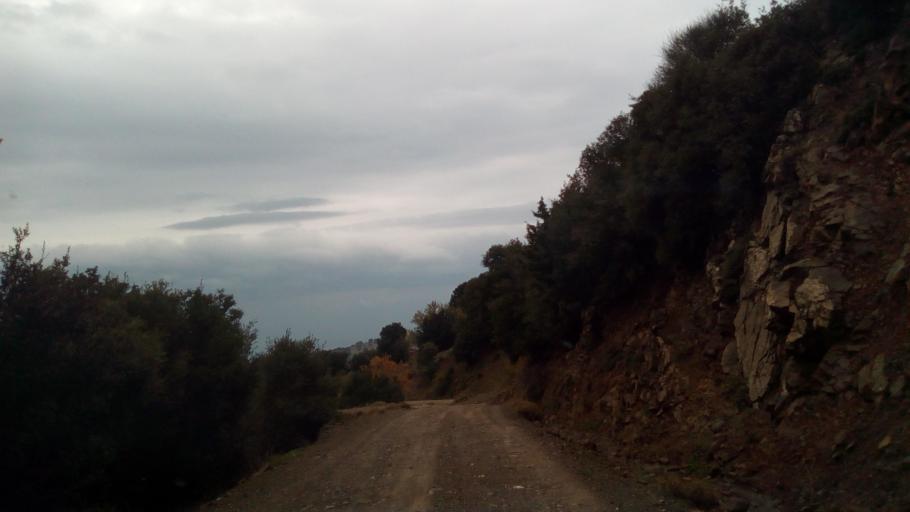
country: GR
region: West Greece
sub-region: Nomos Achaias
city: Selianitika
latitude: 38.4143
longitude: 22.0891
